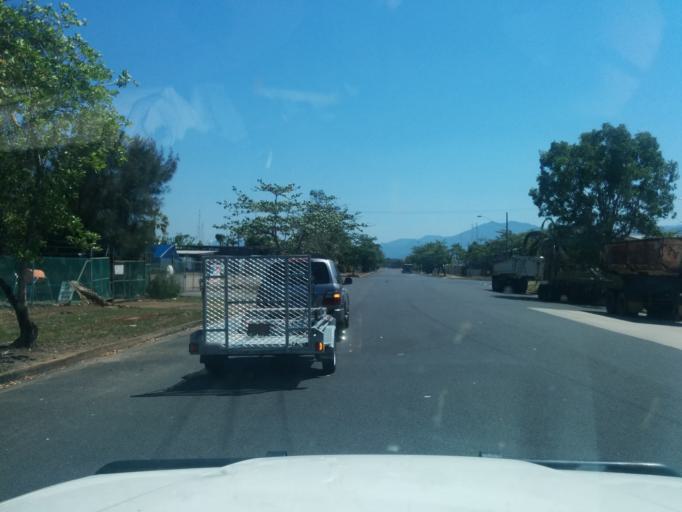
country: AU
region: Queensland
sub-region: Cairns
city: Cairns
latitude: -16.9440
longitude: 145.7729
